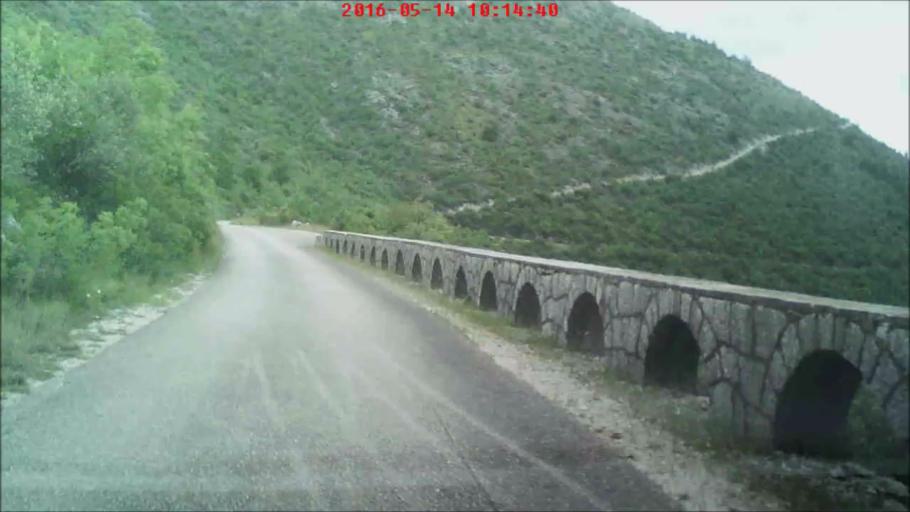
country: HR
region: Dubrovacko-Neretvanska
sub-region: Grad Dubrovnik
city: Mokosica
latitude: 42.7328
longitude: 17.9600
